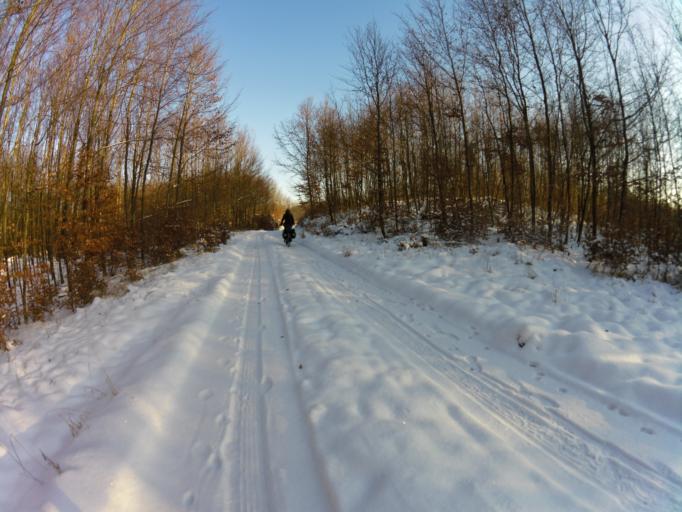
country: PL
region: West Pomeranian Voivodeship
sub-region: Powiat stargardzki
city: Insko
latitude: 53.3819
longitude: 15.5346
